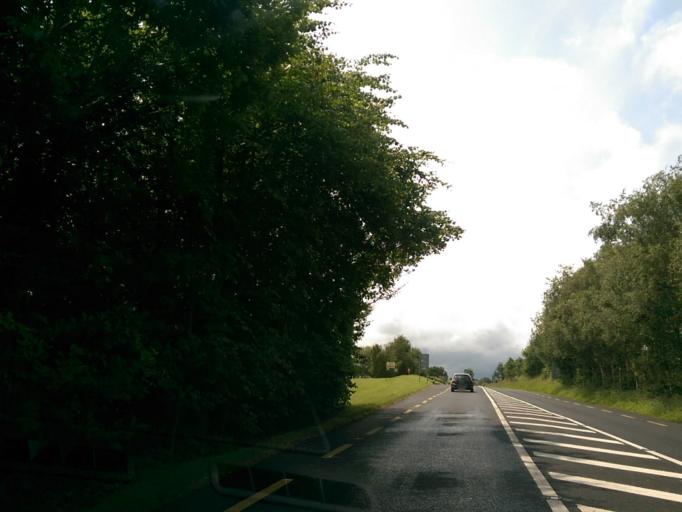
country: IE
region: Munster
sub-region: An Clar
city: Ennis
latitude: 52.8242
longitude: -9.0071
